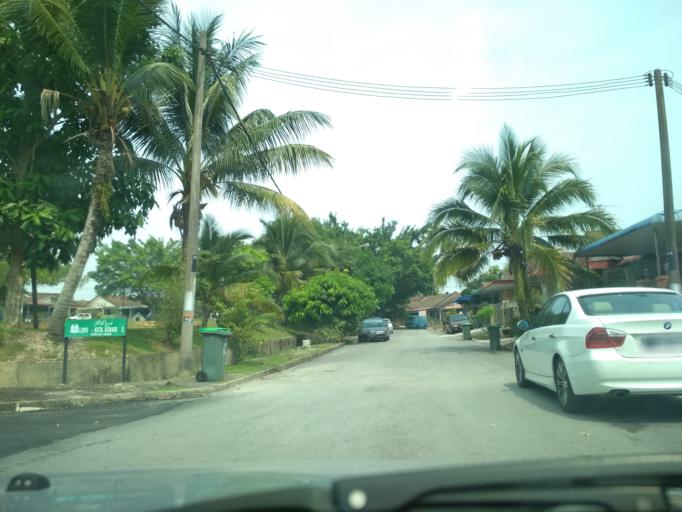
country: MY
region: Kedah
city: Kulim
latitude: 5.3701
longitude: 100.5681
